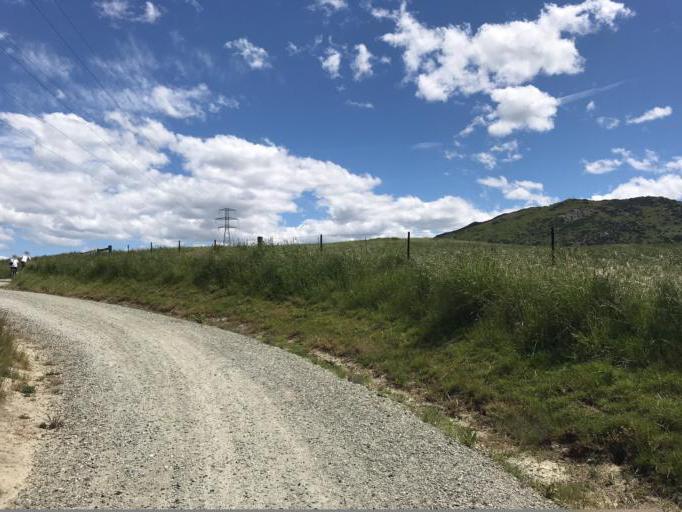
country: NZ
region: Otago
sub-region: Queenstown-Lakes District
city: Arrowtown
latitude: -45.0010
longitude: 168.8483
